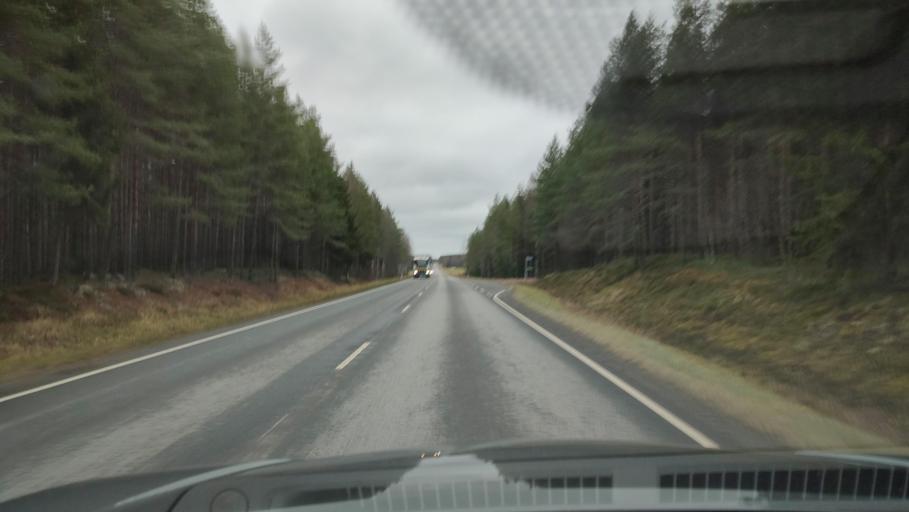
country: FI
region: Southern Ostrobothnia
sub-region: Suupohja
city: Kauhajoki
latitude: 62.4940
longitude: 22.2971
